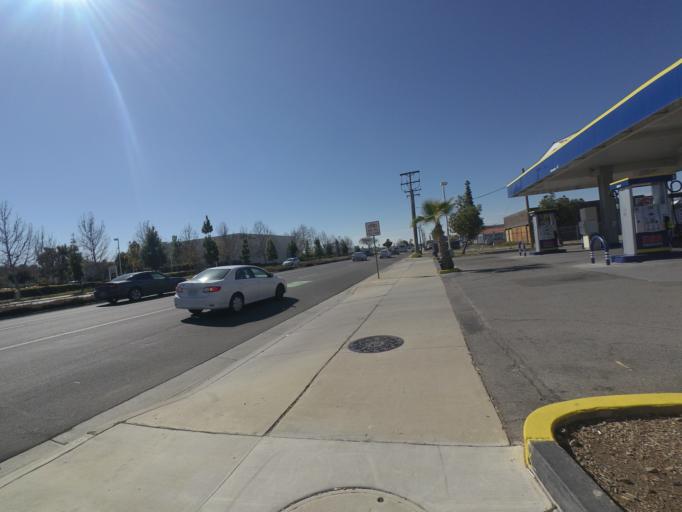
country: US
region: California
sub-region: Riverside County
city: March Air Force Base
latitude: 33.9174
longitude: -117.2614
